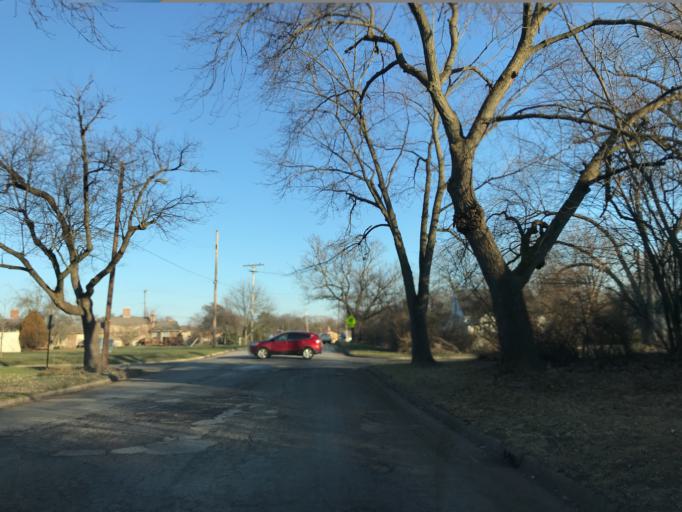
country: US
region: Michigan
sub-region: Washtenaw County
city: Ann Arbor
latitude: 42.2473
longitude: -83.6945
